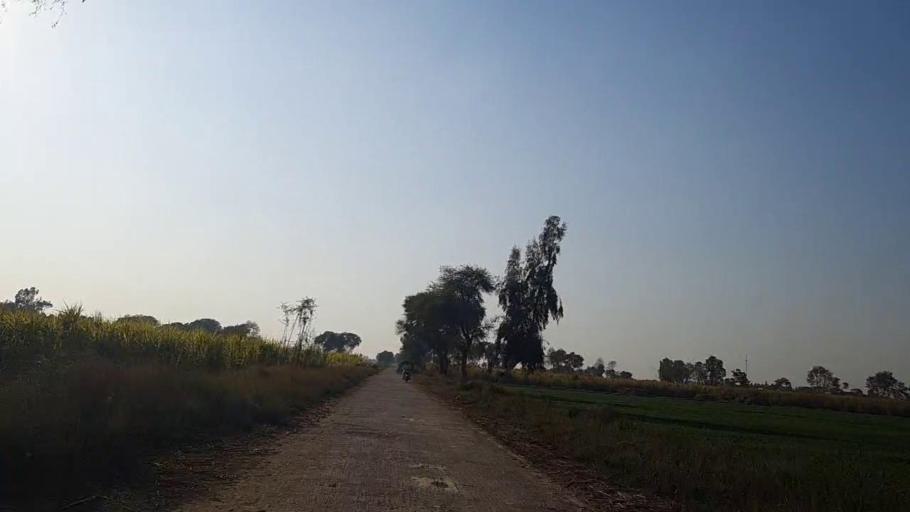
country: PK
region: Sindh
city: Daur
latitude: 26.3329
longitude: 68.1542
